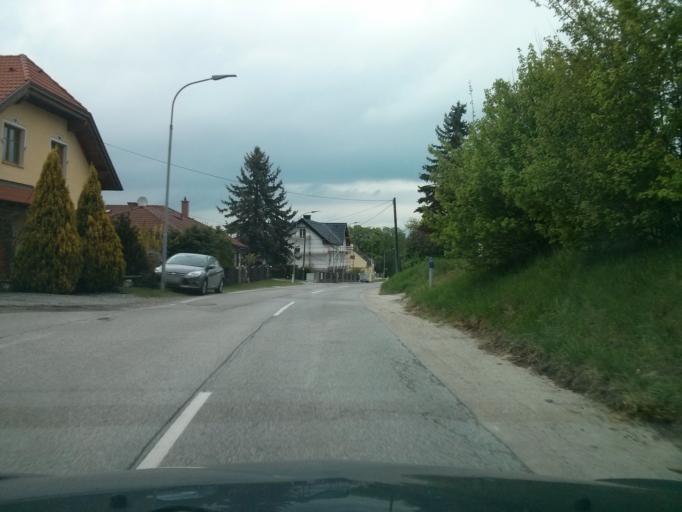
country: AT
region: Lower Austria
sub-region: Politischer Bezirk Baden
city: Hernstein
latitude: 47.9192
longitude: 16.0919
